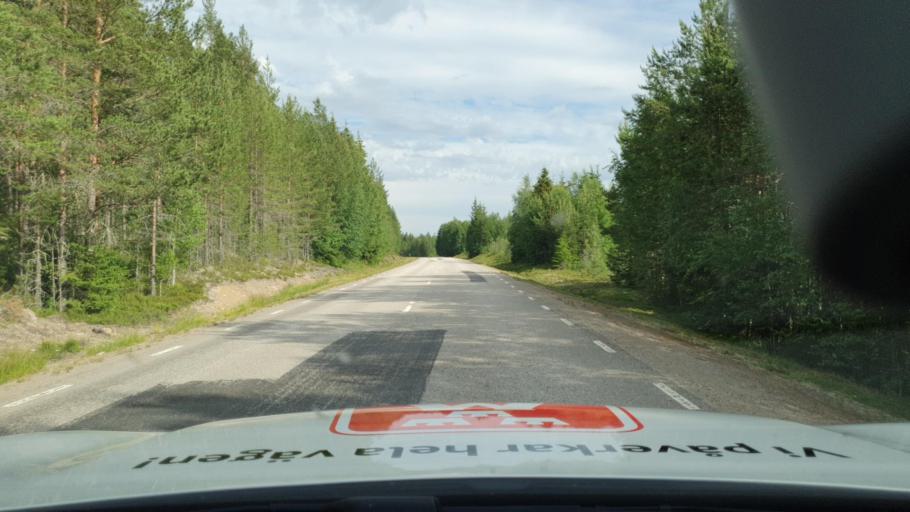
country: NO
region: Hedmark
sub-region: Trysil
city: Innbygda
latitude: 60.9339
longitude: 12.4887
